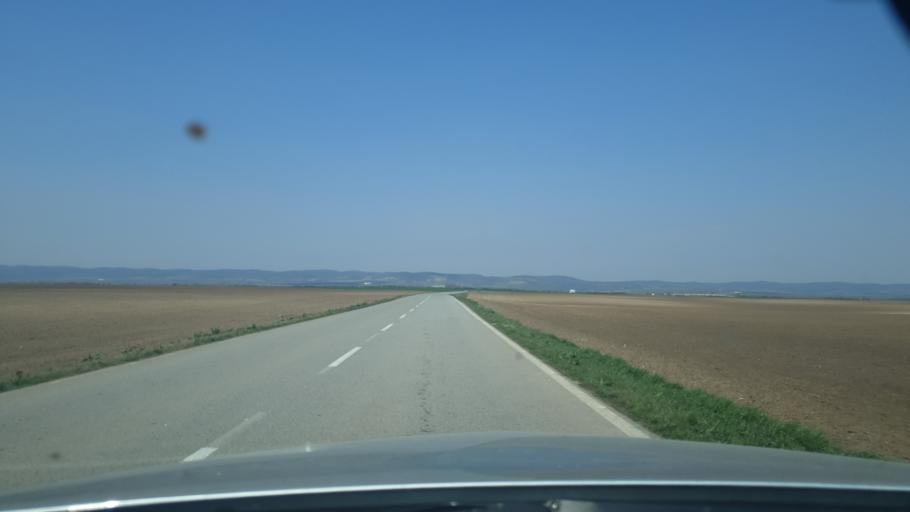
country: RS
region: Autonomna Pokrajina Vojvodina
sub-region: Sremski Okrug
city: Ruma
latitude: 45.0400
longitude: 19.7612
